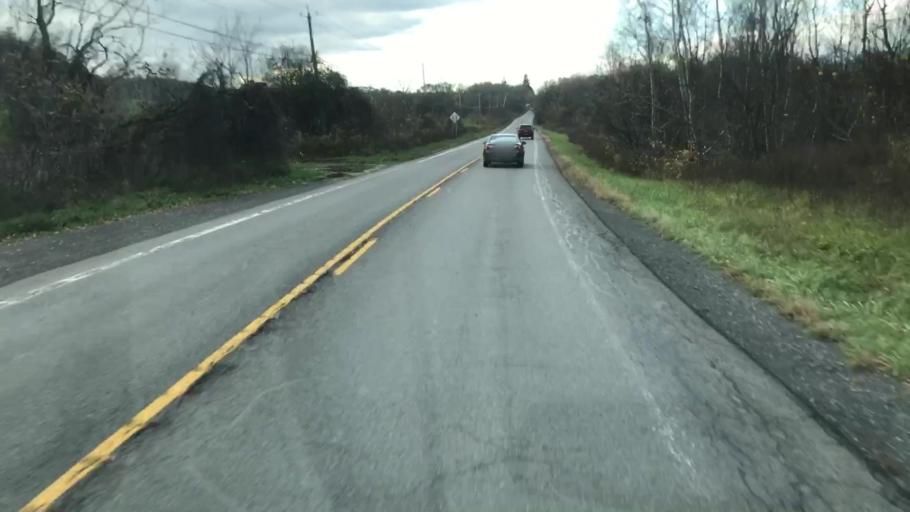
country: US
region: New York
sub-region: Onondaga County
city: Elbridge
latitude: 42.9985
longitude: -76.4255
